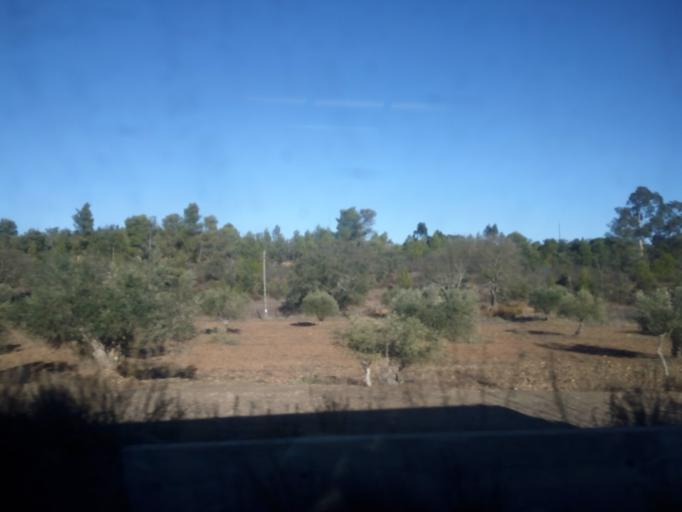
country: PT
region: Faro
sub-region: Silves
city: Sao Bartolomeu de Messines
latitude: 37.3384
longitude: -8.3508
